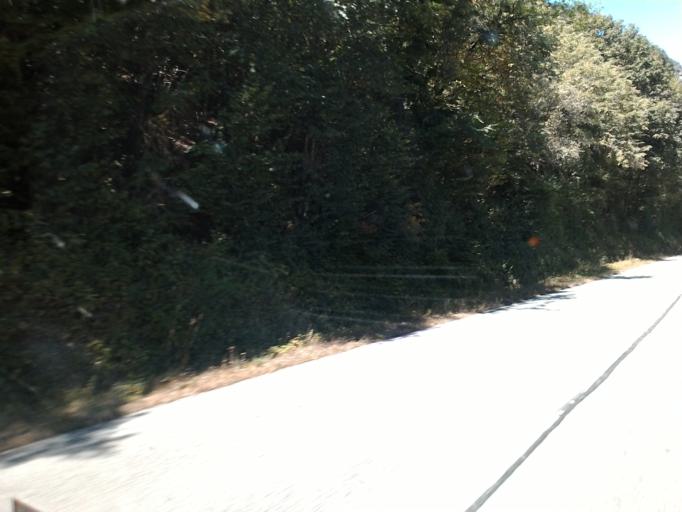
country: FR
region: Rhone-Alpes
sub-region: Departement de l'Ain
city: Saint-Sorlin-en-Bugey
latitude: 45.8647
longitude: 5.3826
